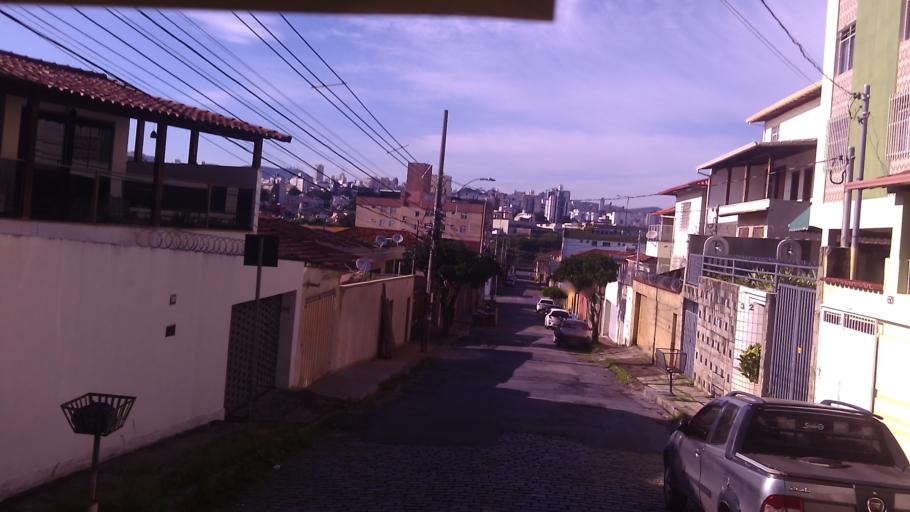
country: BR
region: Minas Gerais
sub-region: Belo Horizonte
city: Belo Horizonte
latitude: -19.9180
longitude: -43.9718
